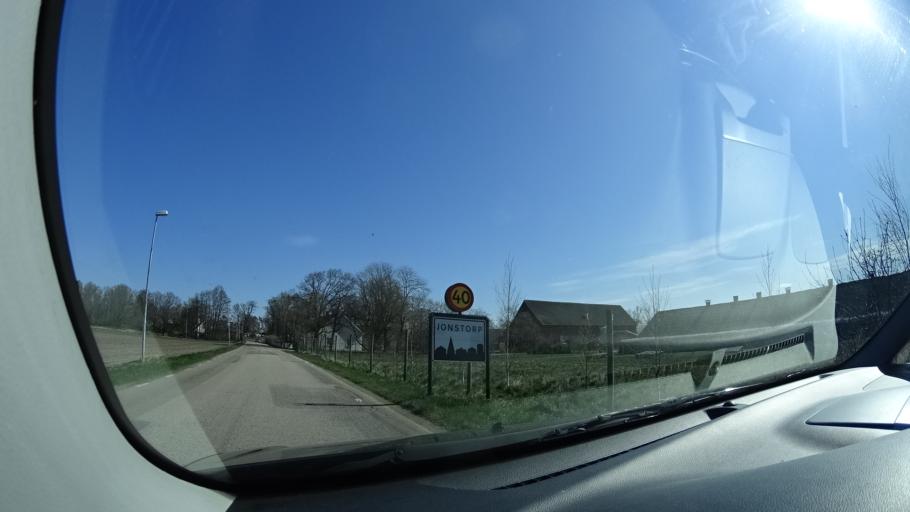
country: SE
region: Skane
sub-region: Hoganas Kommun
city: Hoganas
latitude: 56.2167
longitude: 12.6665
